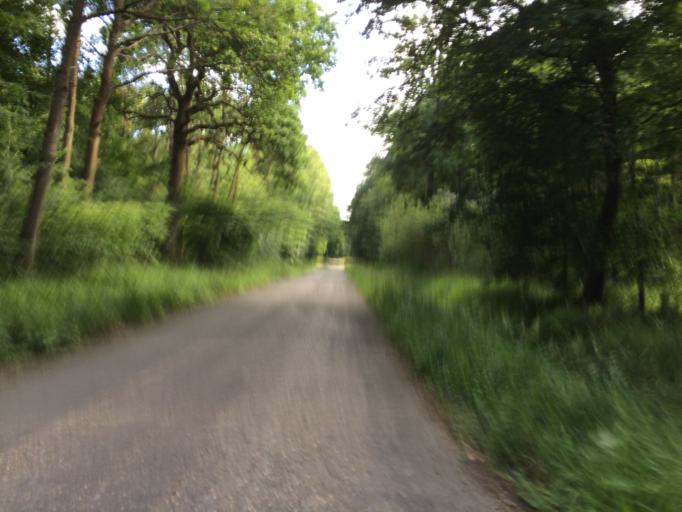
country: FR
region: Ile-de-France
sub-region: Departement de l'Essonne
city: Etiolles
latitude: 48.6634
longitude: 2.4840
